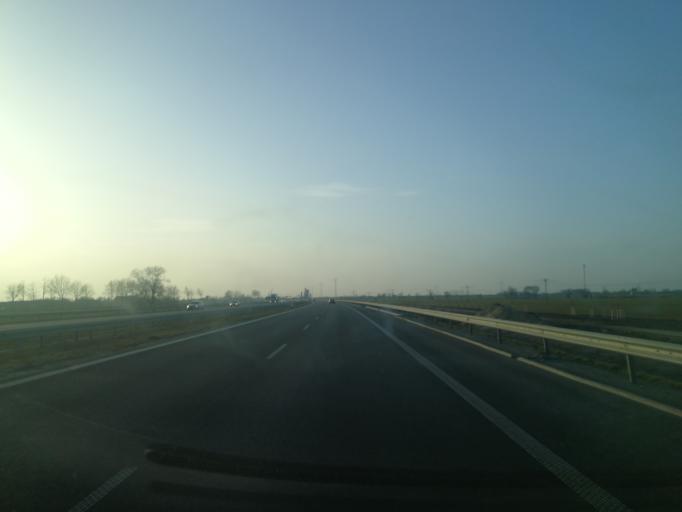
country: PL
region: Pomeranian Voivodeship
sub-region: Powiat nowodworski
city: Ostaszewo
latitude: 54.2528
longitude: 18.9779
